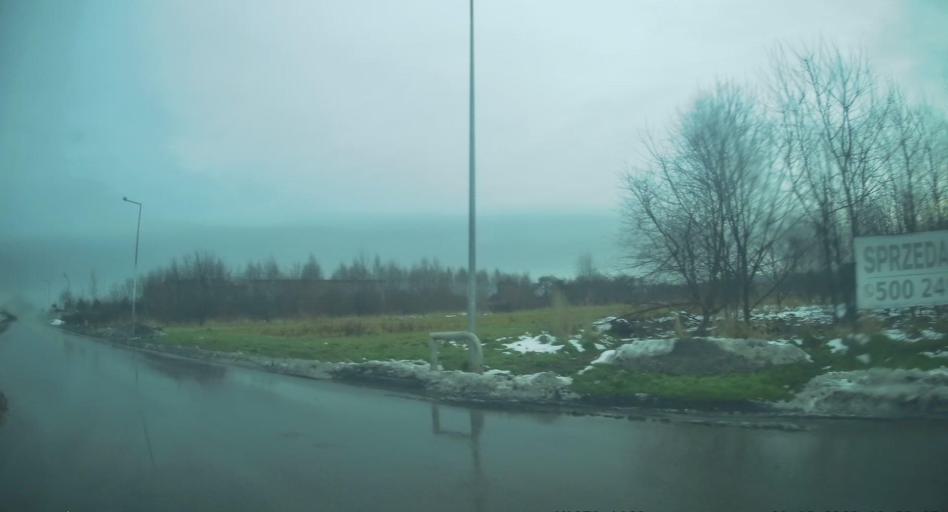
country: PL
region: Lodz Voivodeship
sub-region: Powiat radomszczanski
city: Radomsko
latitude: 51.0817
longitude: 19.3771
